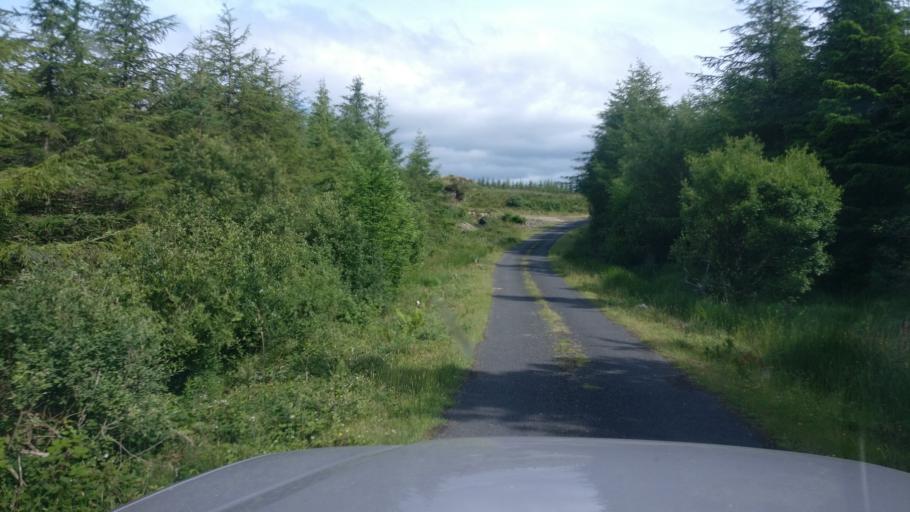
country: IE
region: Connaught
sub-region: County Galway
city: Gort
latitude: 53.0837
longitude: -8.6916
